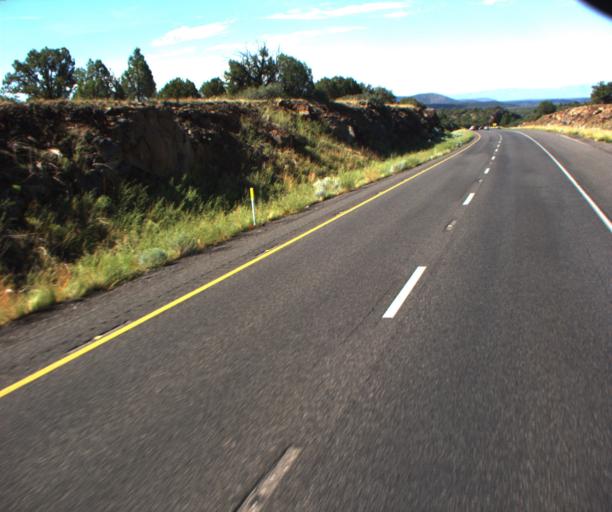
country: US
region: Arizona
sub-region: Yavapai County
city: Village of Oak Creek (Big Park)
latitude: 34.7972
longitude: -111.5994
